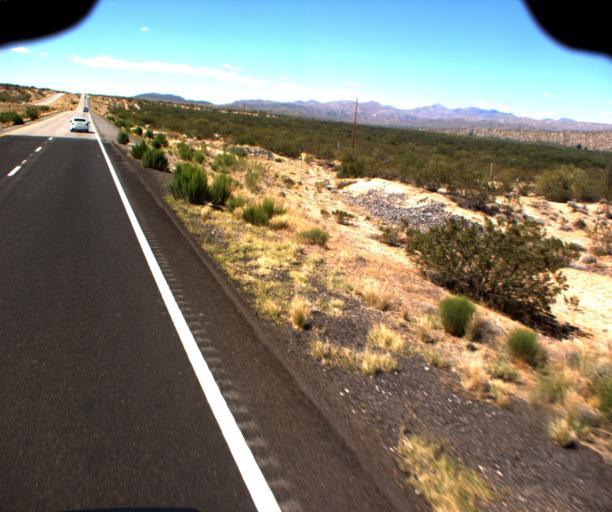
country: US
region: Arizona
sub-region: Mohave County
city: Kingman
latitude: 34.8534
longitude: -113.6386
